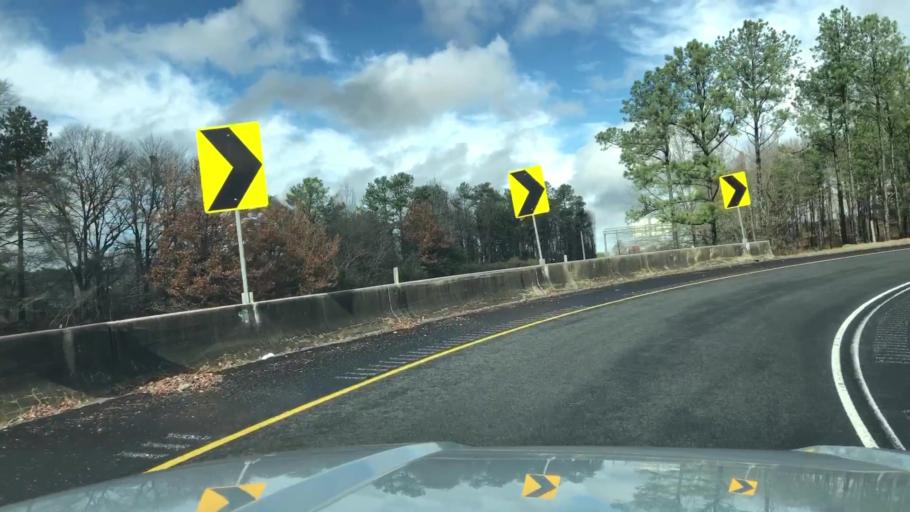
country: US
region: Georgia
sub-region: Fulton County
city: College Park
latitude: 33.6191
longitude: -84.4890
